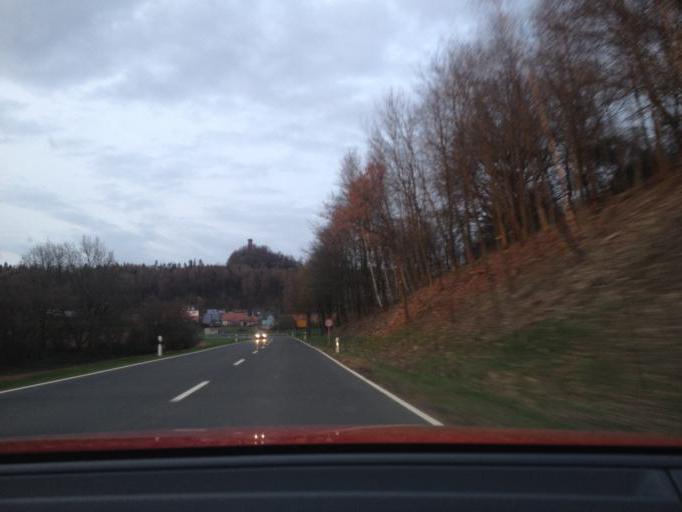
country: DE
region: Bavaria
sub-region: Upper Palatinate
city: Speinshart
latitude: 49.8216
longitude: 11.8390
